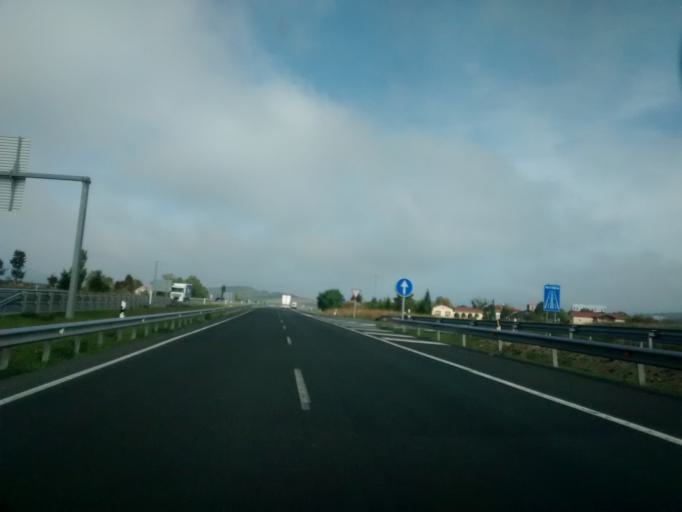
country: ES
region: Basque Country
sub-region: Provincia de Alava
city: Gasteiz / Vitoria
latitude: 42.9126
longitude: -2.6475
